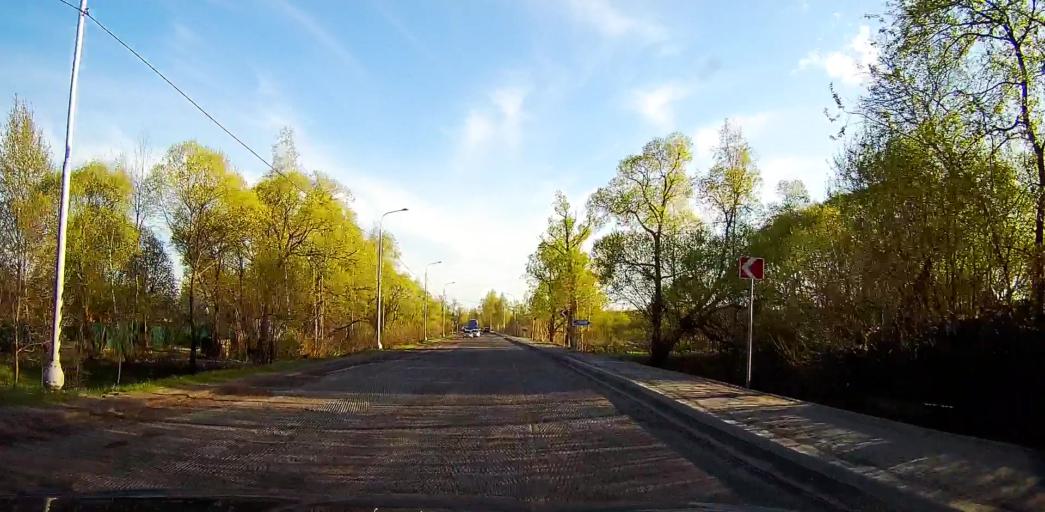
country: RU
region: Moskovskaya
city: Bronnitsy
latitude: 55.3038
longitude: 38.2111
